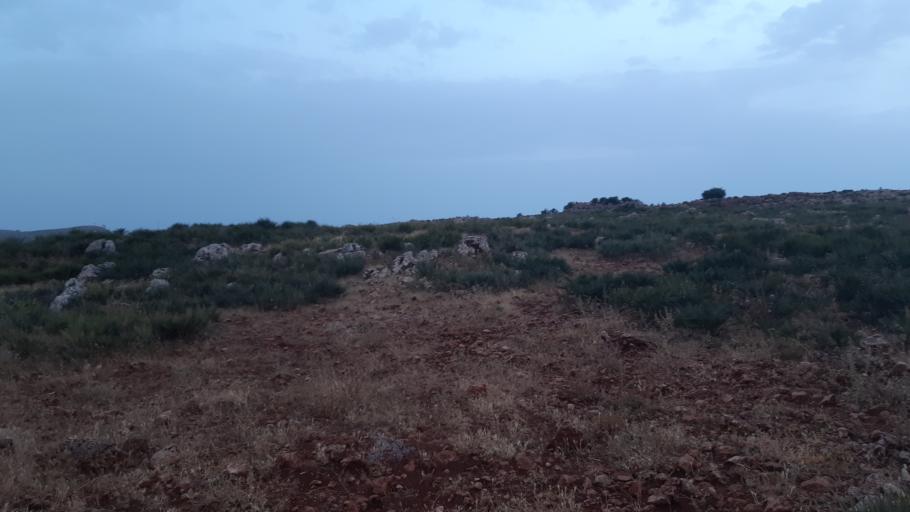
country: MA
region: Meknes-Tafilalet
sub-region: El-Hajeb
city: El Hajeb
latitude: 33.6716
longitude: -5.3925
